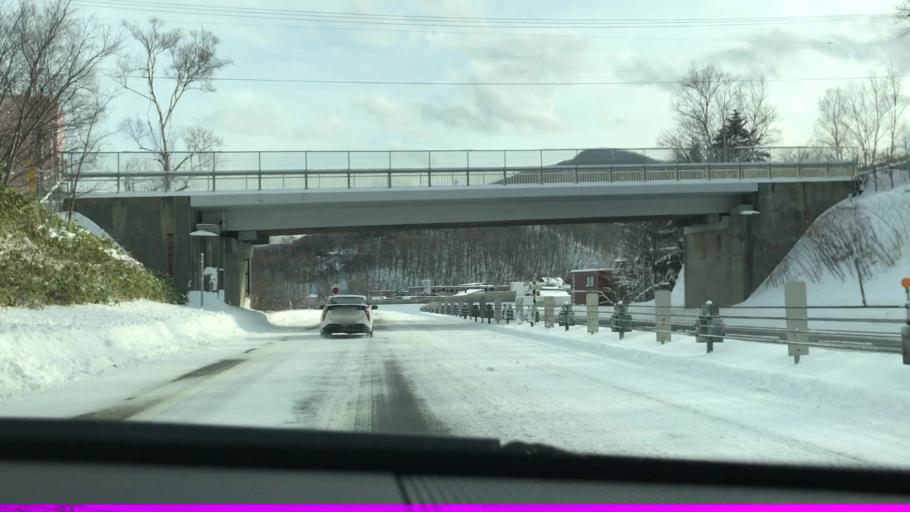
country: JP
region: Hokkaido
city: Otaru
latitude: 43.1429
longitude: 141.1434
